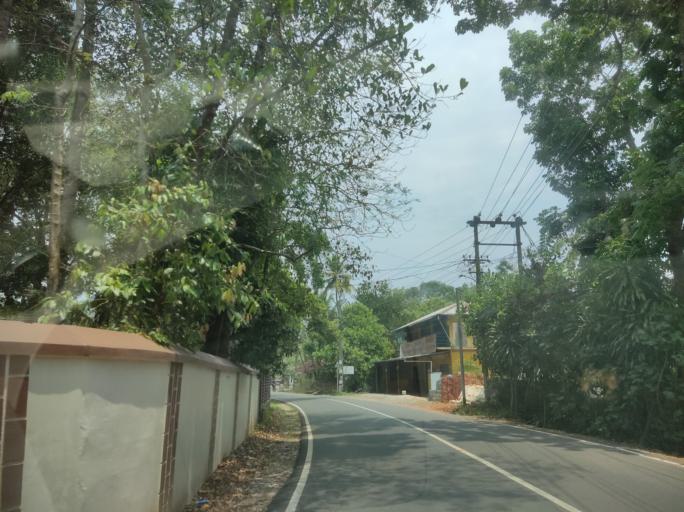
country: IN
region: Kerala
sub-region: Alappuzha
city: Vayalar
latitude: 9.7146
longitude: 76.3274
